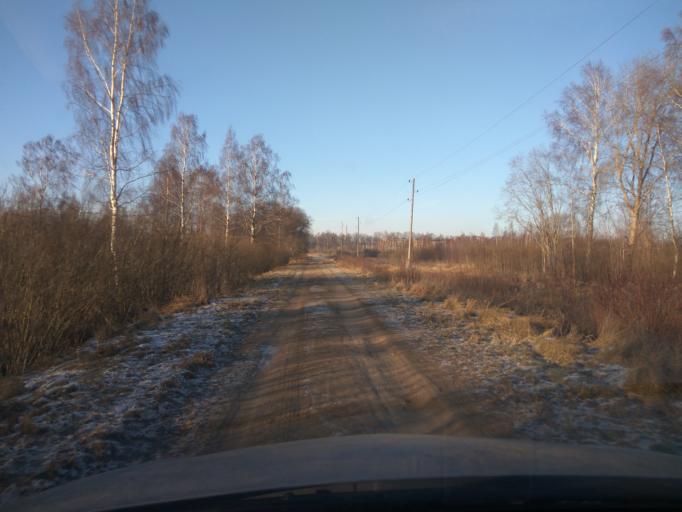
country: LV
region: Kuldigas Rajons
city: Kuldiga
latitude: 56.9622
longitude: 21.9599
